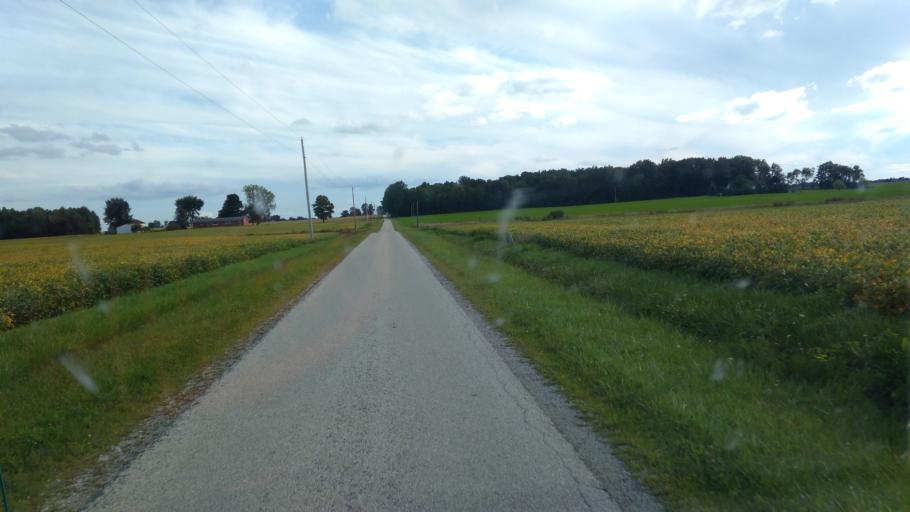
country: US
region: Ohio
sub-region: Crawford County
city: Bucyrus
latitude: 40.9189
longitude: -82.9782
